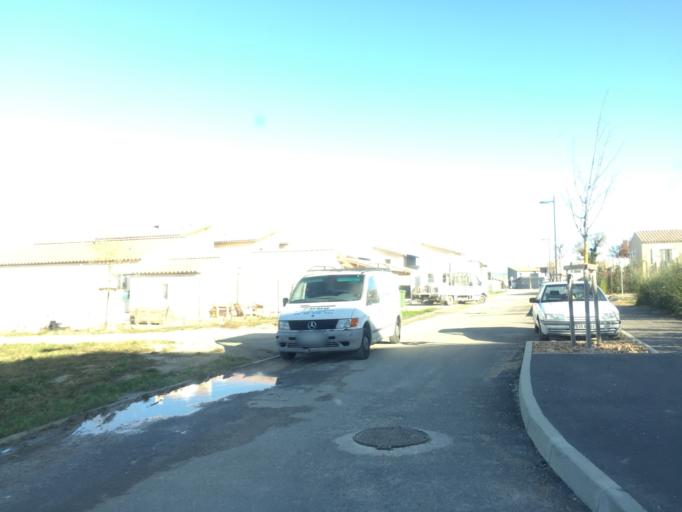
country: FR
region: Provence-Alpes-Cote d'Azur
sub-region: Departement du Vaucluse
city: Bedarrides
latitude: 44.0332
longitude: 4.8953
